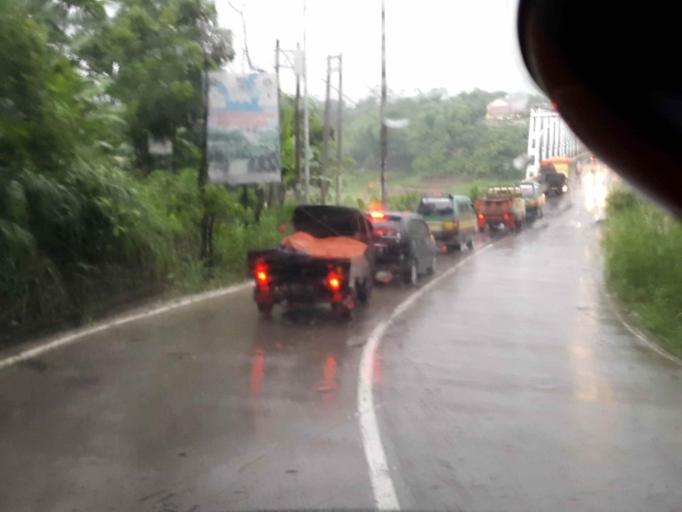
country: ID
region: West Java
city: Cimahi
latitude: -6.9319
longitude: 107.5061
